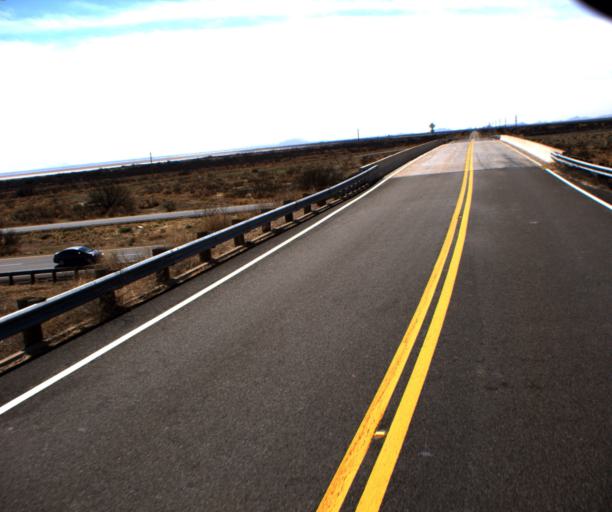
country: US
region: Arizona
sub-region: Cochise County
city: Willcox
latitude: 32.1770
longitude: -109.9498
